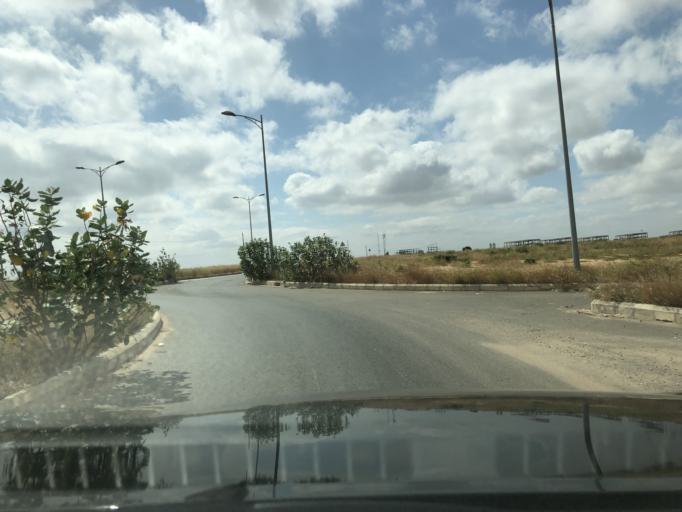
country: AO
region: Luanda
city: Luanda
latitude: -8.9644
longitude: 13.2448
